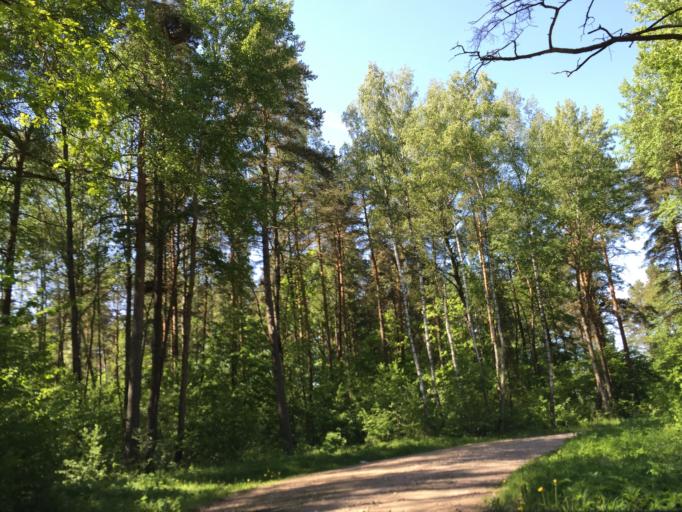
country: LV
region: Bauskas Rajons
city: Bauska
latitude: 56.4246
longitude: 24.2973
